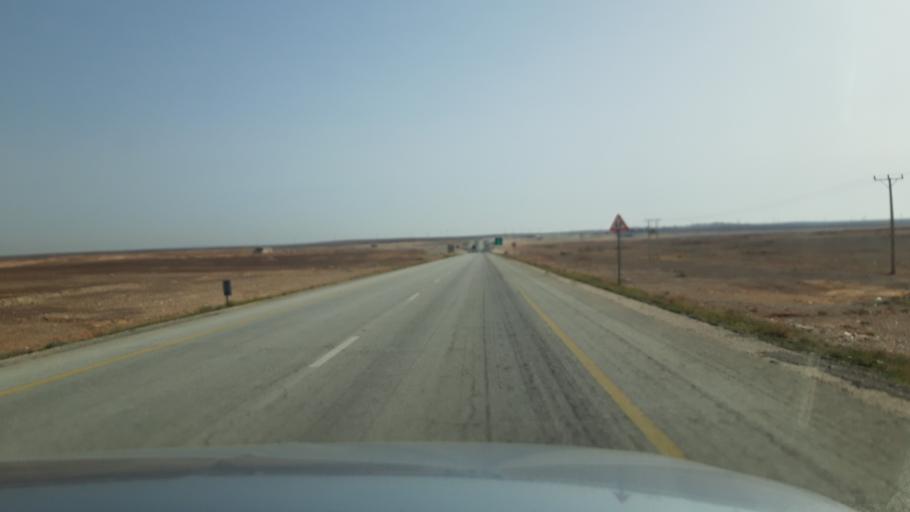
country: JO
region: Amman
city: Al Azraq ash Shamali
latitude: 31.8682
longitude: 36.7211
